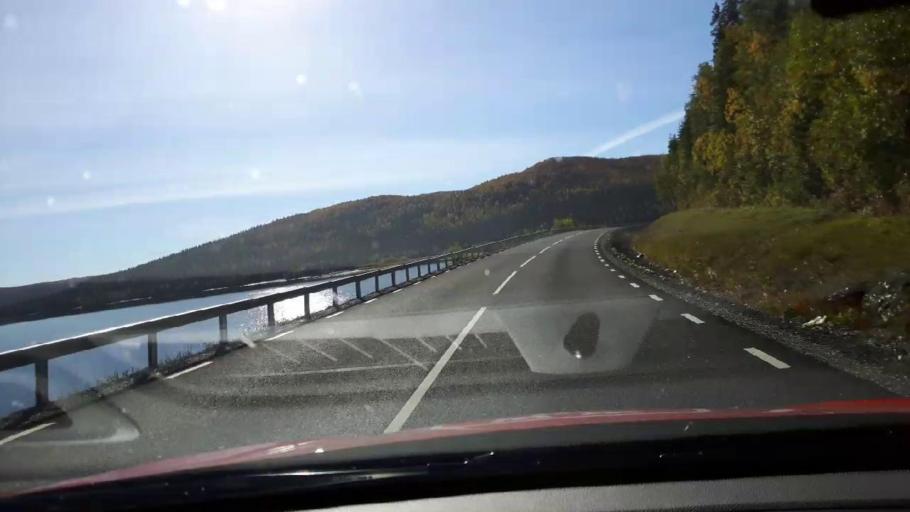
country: NO
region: Nord-Trondelag
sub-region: Royrvik
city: Royrvik
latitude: 64.8246
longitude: 14.0769
